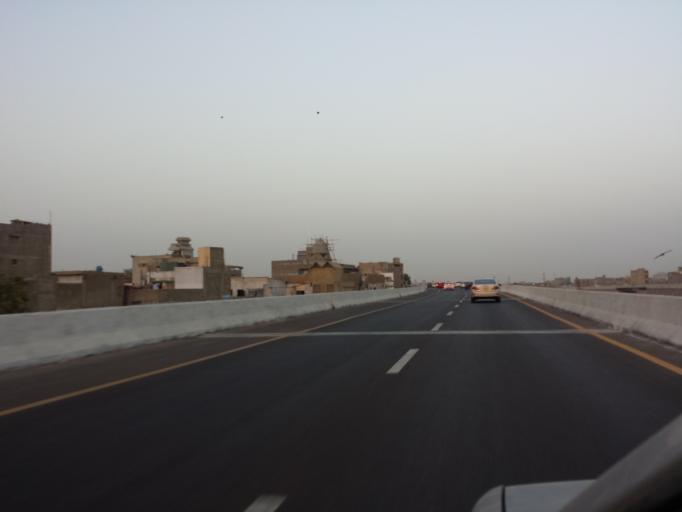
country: PK
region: Sindh
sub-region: Karachi District
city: Karachi
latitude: 24.8985
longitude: 67.0566
